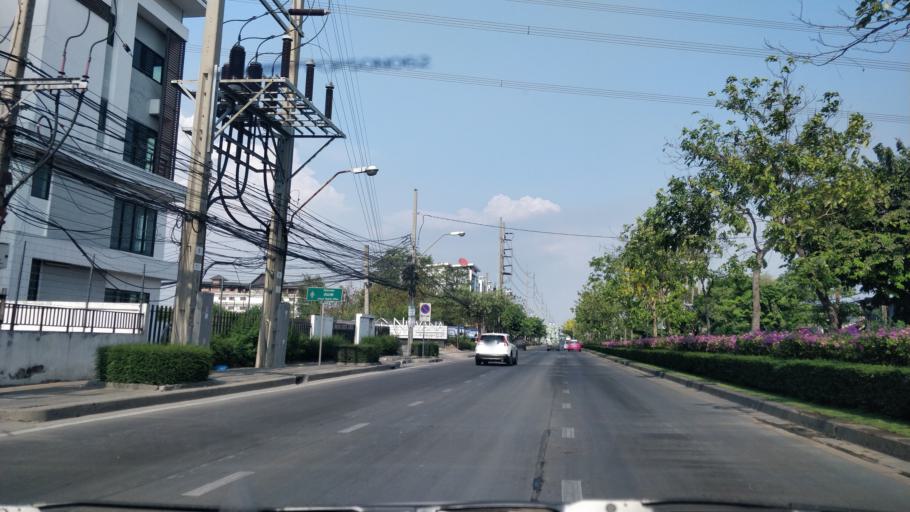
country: TH
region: Bangkok
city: Suan Luang
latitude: 13.7207
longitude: 100.6849
